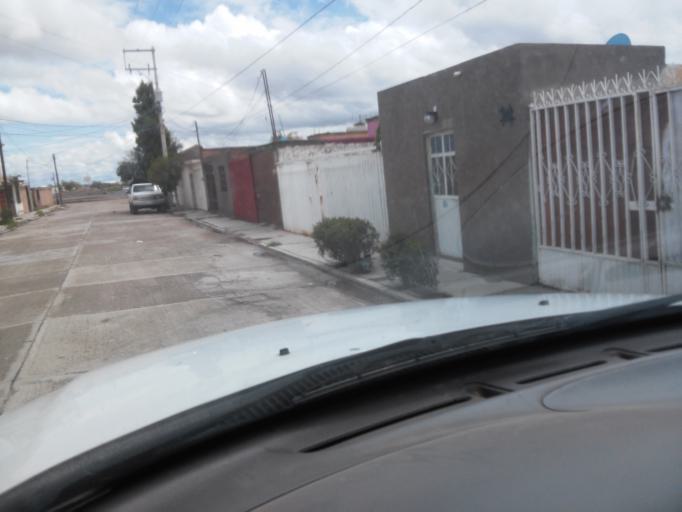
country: MX
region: Durango
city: Victoria de Durango
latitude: 24.0238
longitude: -104.6160
